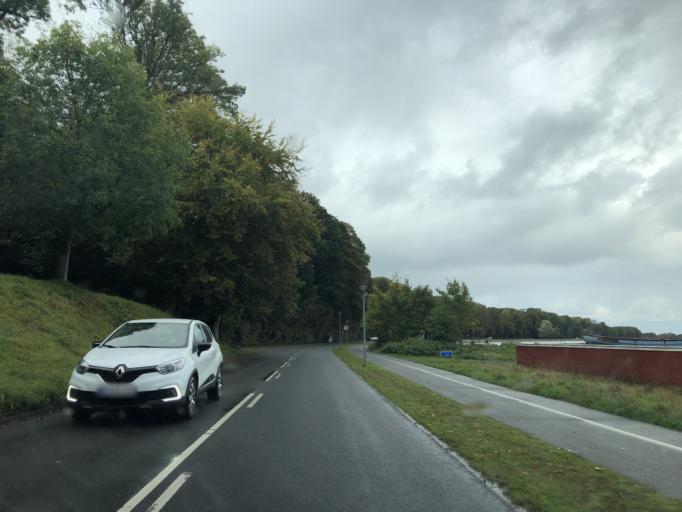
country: DK
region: Central Jutland
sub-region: Lemvig Kommune
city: Lemvig
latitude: 56.5508
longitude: 8.2989
